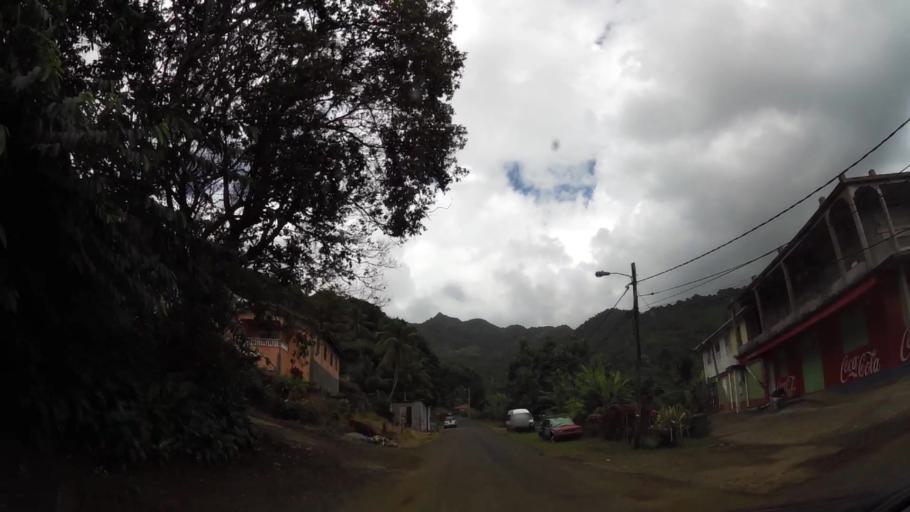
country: DM
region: Saint David
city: Castle Bruce
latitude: 15.4414
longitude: -61.2608
